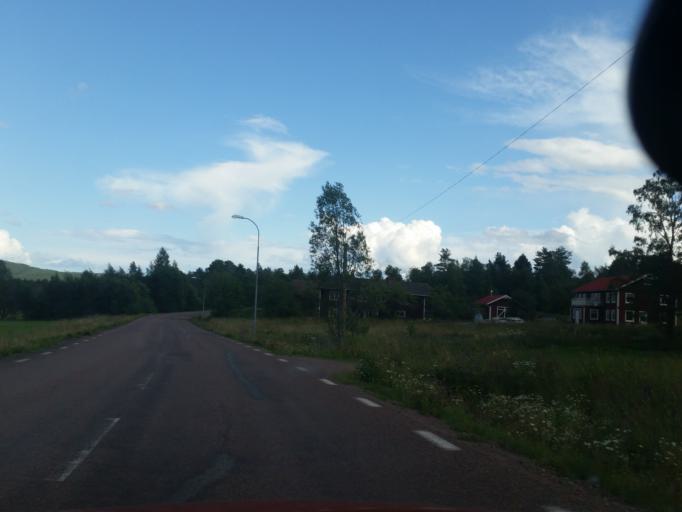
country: SE
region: Dalarna
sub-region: Leksand Municipality
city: Smedby
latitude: 60.6779
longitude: 15.1226
